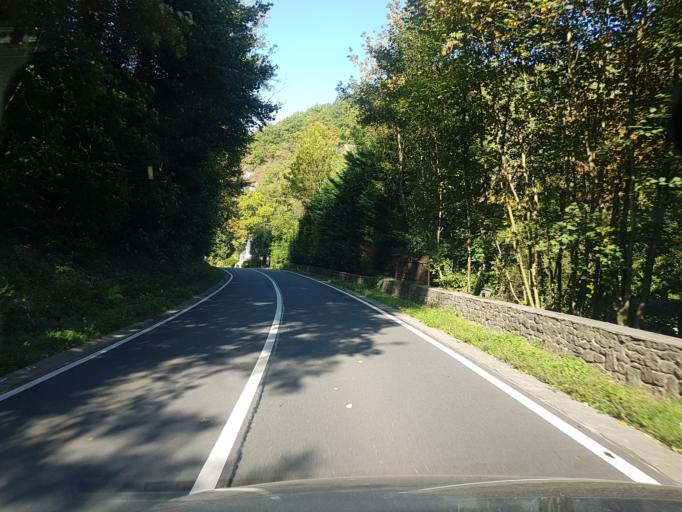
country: BE
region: Wallonia
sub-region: Province de Namur
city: Gesves
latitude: 50.4526
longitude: 5.0109
